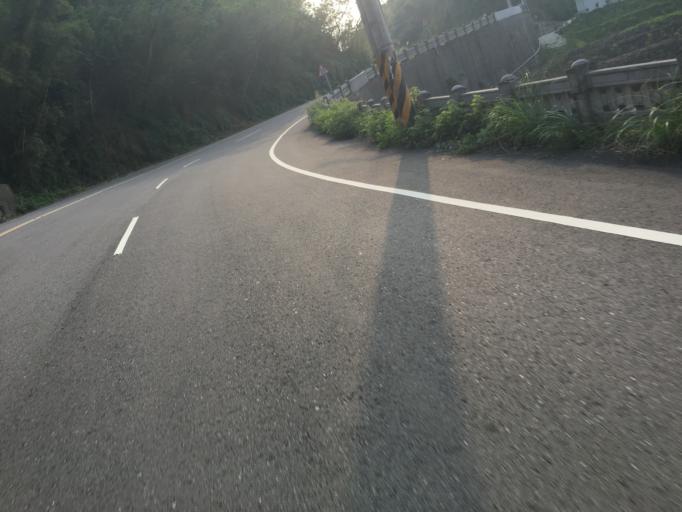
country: TW
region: Taiwan
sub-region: Hsinchu
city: Hsinchu
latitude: 24.7263
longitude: 121.0345
